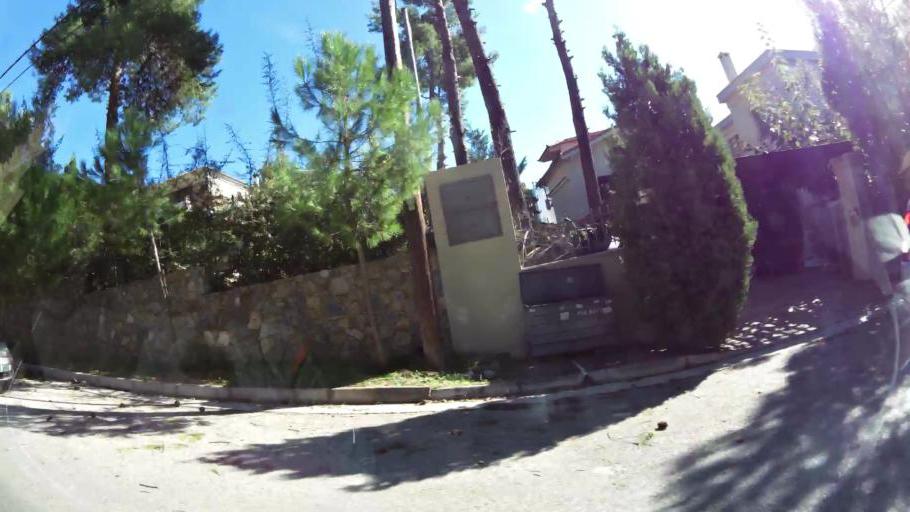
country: GR
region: Attica
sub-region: Nomarchia Anatolikis Attikis
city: Dionysos
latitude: 38.1078
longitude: 23.8836
